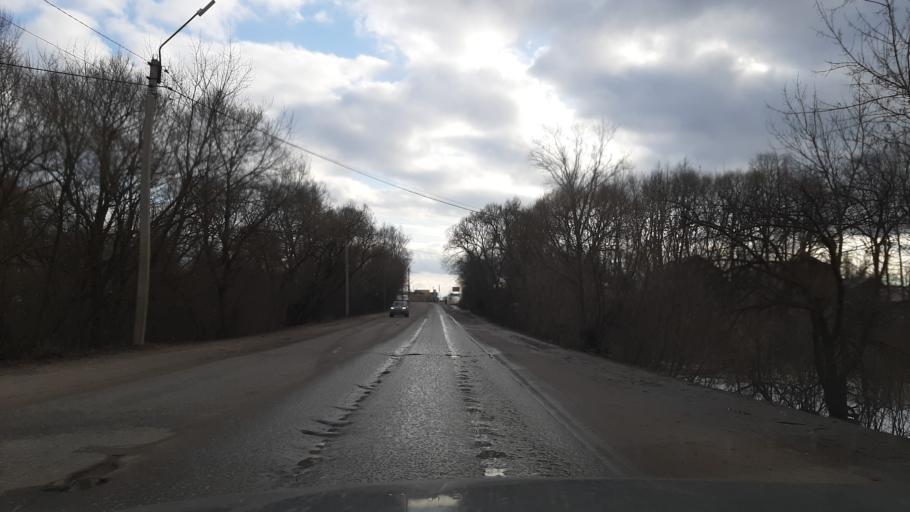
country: RU
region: Ivanovo
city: Teykovo
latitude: 56.8571
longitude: 40.5195
